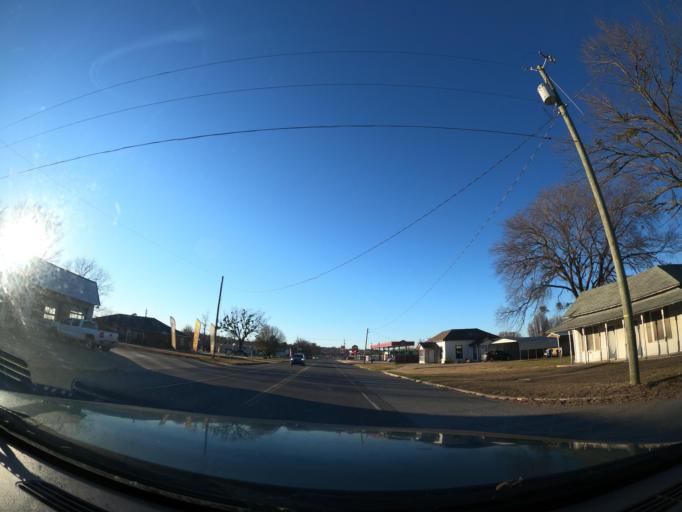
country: US
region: Oklahoma
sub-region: Pittsburg County
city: Hartshorne
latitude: 34.8462
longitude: -95.5600
